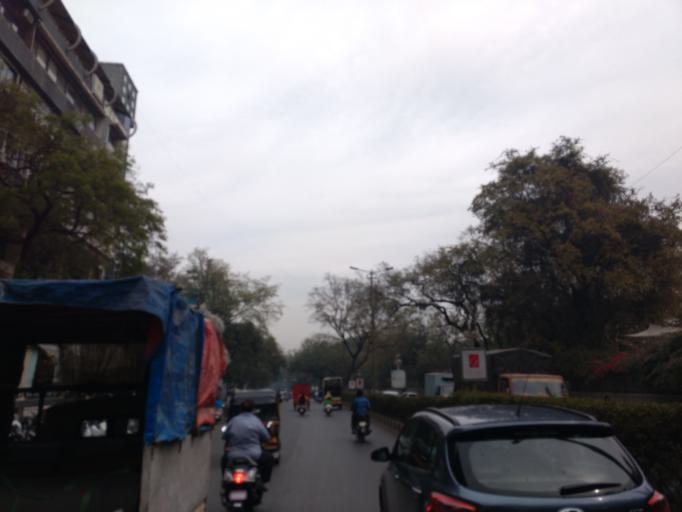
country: IN
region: Maharashtra
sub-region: Pune Division
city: Pune
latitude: 18.5221
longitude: 73.8779
